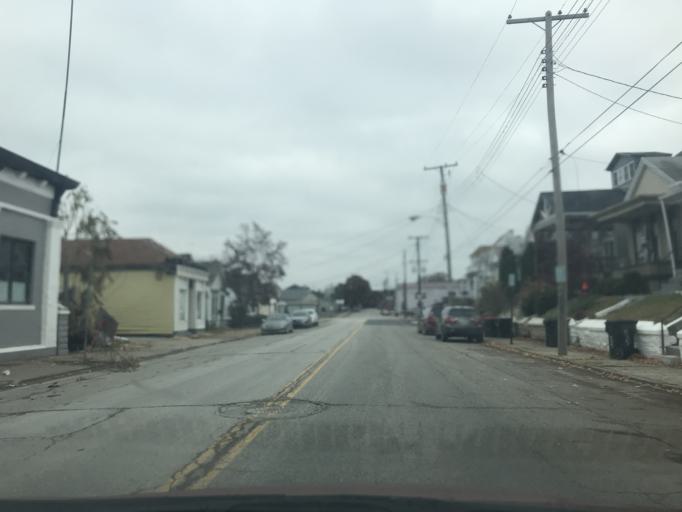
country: US
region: Kentucky
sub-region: Jefferson County
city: Louisville
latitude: 38.2460
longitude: -85.7322
